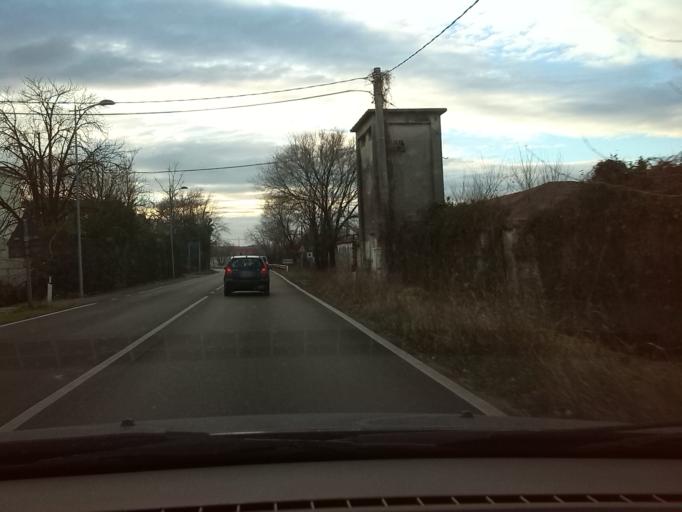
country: IT
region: Friuli Venezia Giulia
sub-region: Provincia di Gorizia
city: Sagrado
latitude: 45.8908
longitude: 13.4772
